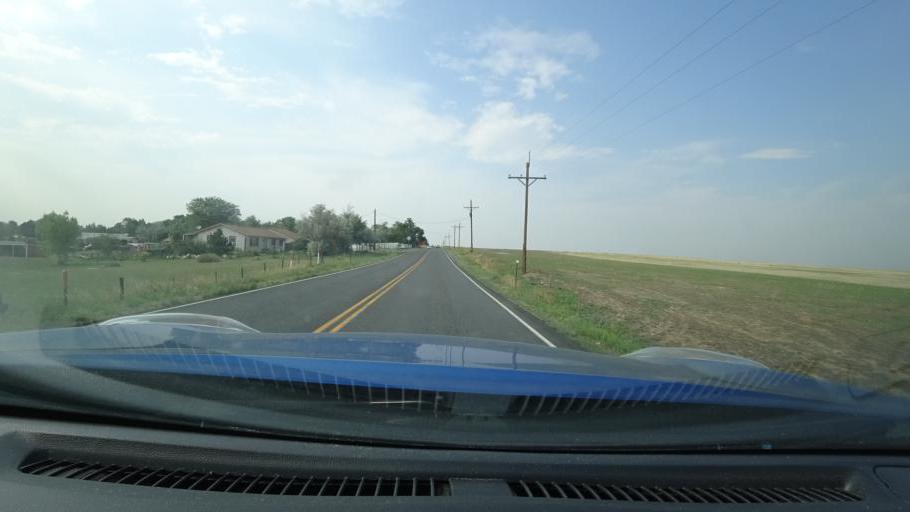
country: US
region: Colorado
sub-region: Adams County
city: Aurora
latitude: 39.7290
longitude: -104.7349
